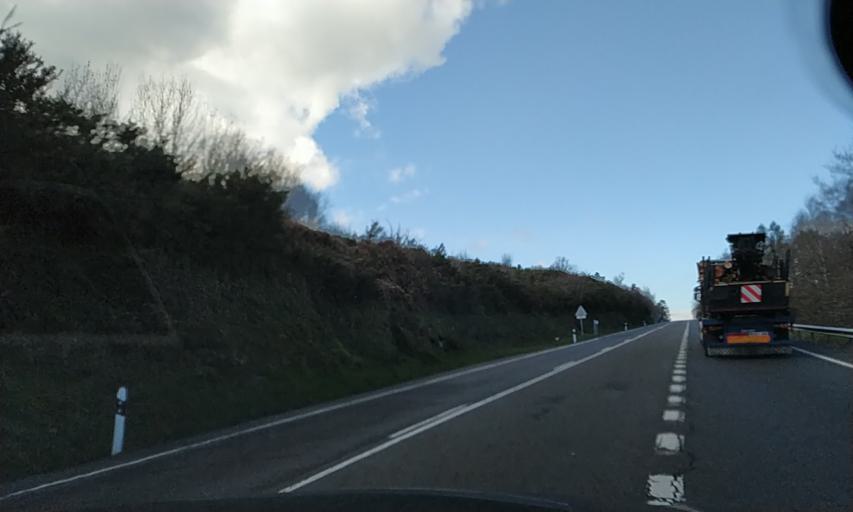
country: ES
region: Galicia
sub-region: Provincia de Pontevedra
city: Silleda
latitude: 42.7013
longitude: -8.3403
